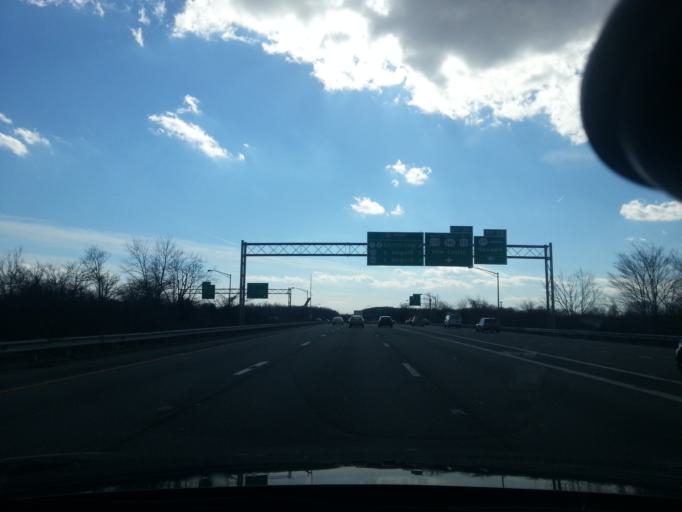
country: US
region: Delaware
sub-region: New Castle County
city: Newport
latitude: 39.7072
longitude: -75.5982
